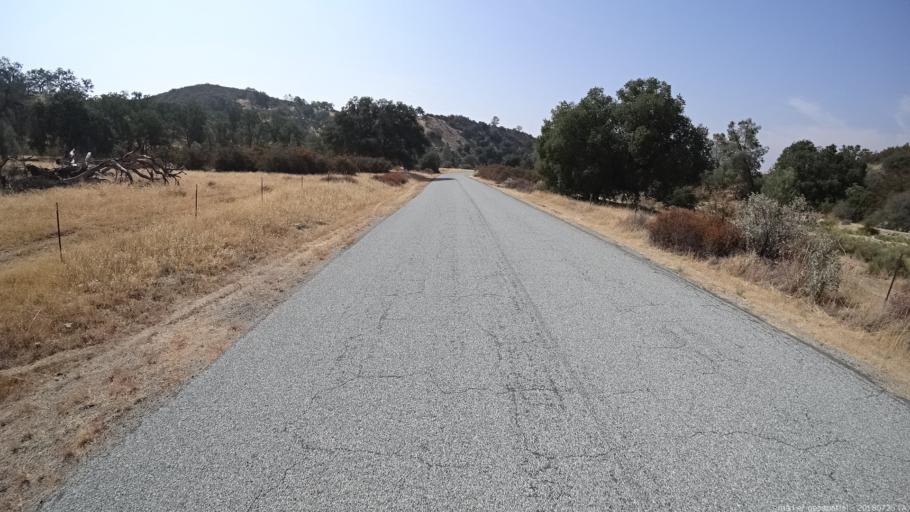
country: US
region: California
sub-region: San Luis Obispo County
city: San Miguel
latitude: 35.8885
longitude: -120.5592
